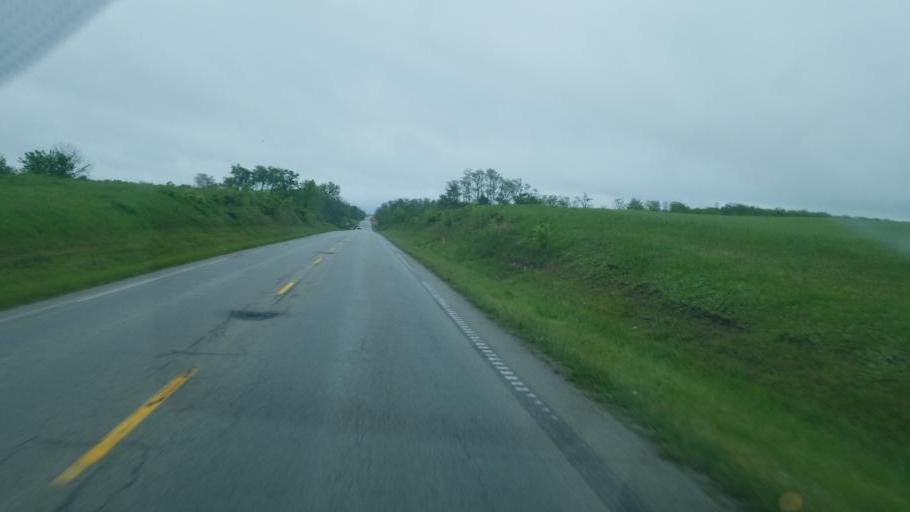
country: US
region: Ohio
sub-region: Highland County
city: Leesburg
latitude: 39.2947
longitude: -83.5875
